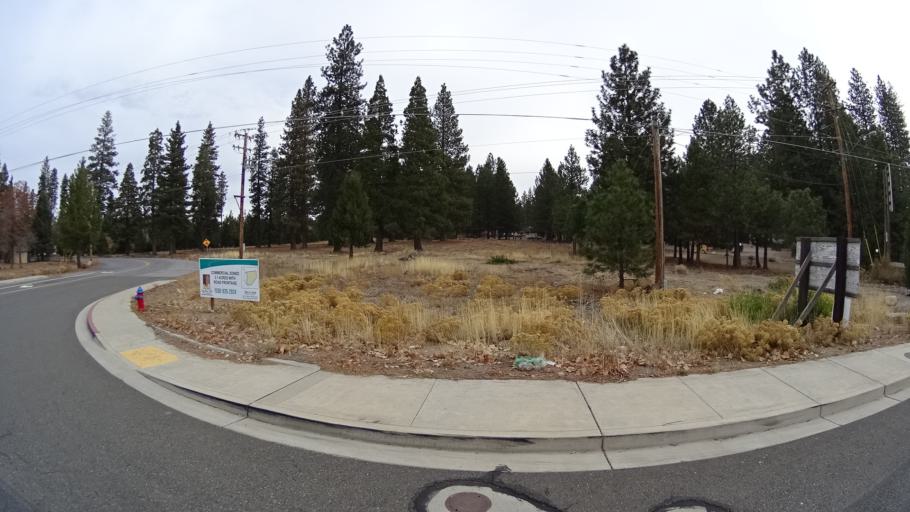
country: US
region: California
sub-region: Siskiyou County
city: Weed
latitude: 41.3997
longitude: -122.3796
